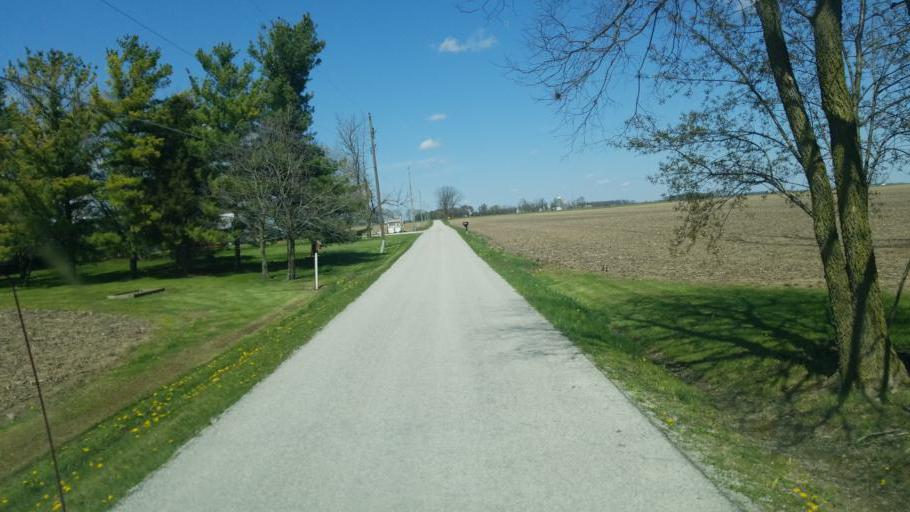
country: US
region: Ohio
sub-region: Marion County
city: Prospect
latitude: 40.3896
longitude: -83.1304
